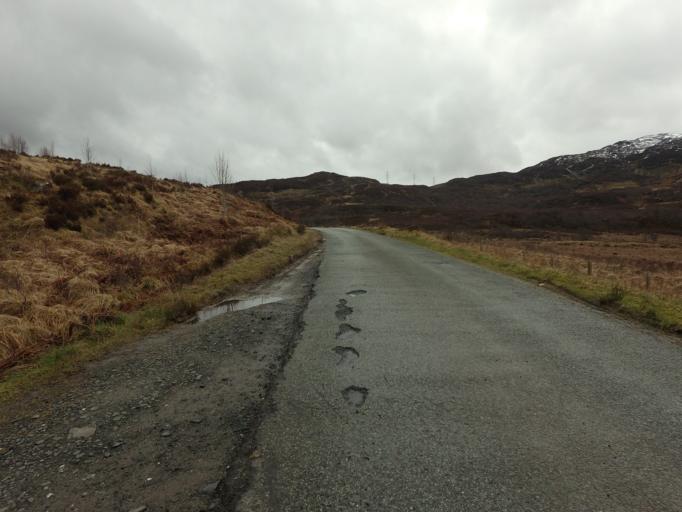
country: GB
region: Scotland
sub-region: West Dunbartonshire
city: Balloch
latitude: 56.2478
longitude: -4.5858
